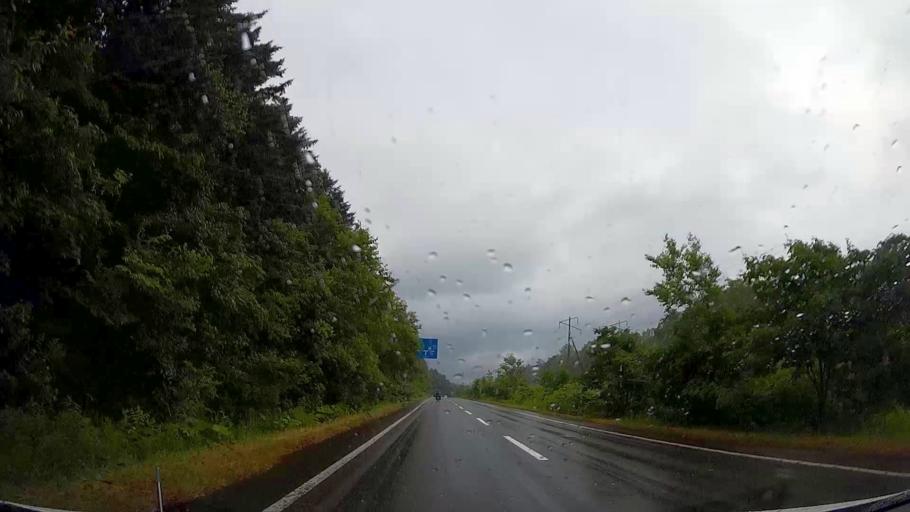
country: JP
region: Hokkaido
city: Tomakomai
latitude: 42.7609
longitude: 141.4370
